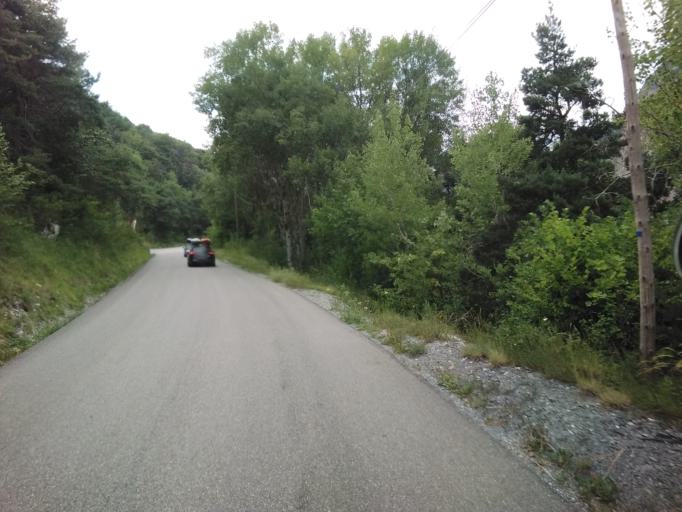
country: FR
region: Provence-Alpes-Cote d'Azur
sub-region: Departement des Alpes-de-Haute-Provence
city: Seyne-les-Alpes
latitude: 44.4477
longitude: 6.4054
